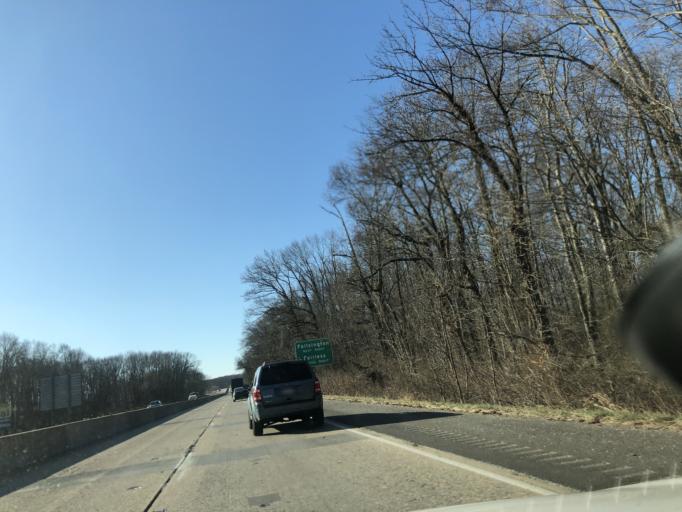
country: US
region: Pennsylvania
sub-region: Bucks County
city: Morrisville
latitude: 40.1859
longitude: -74.8038
